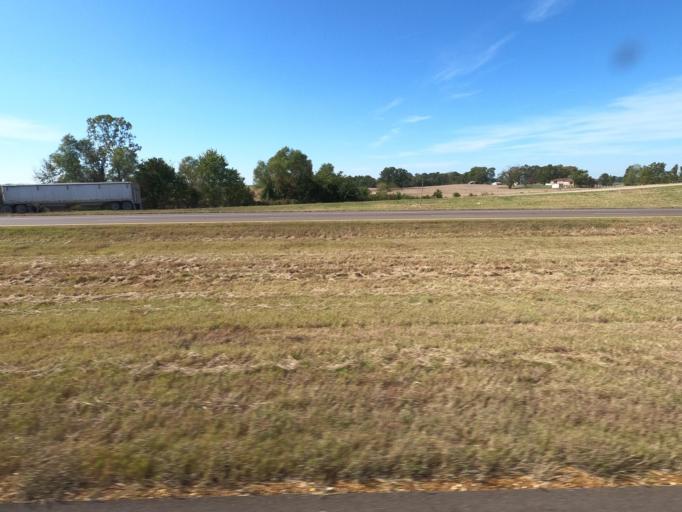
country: US
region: Tennessee
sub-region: Obion County
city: Obion
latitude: 36.2600
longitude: -89.2167
